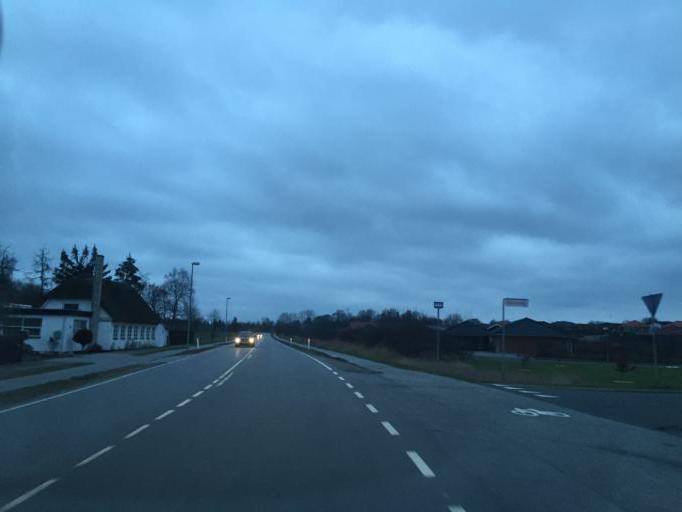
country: DK
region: South Denmark
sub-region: Haderslev Kommune
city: Starup
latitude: 55.2548
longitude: 9.5254
